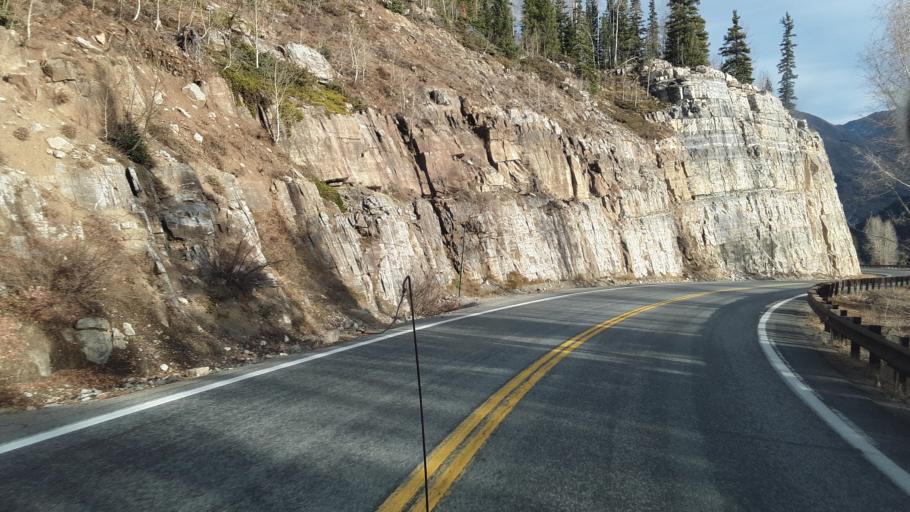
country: US
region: Colorado
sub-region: San Juan County
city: Silverton
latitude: 37.7801
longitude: -107.6726
